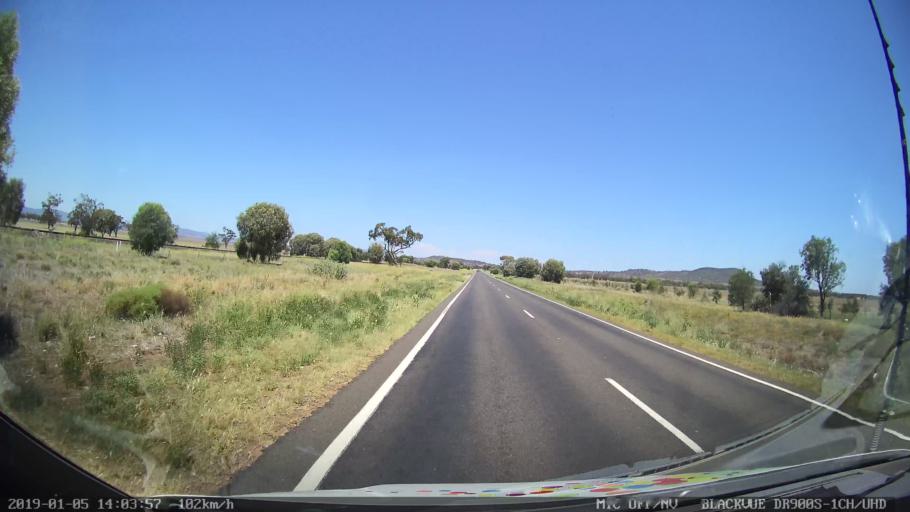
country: AU
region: New South Wales
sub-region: Gunnedah
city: Gunnedah
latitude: -31.1951
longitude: 150.3576
